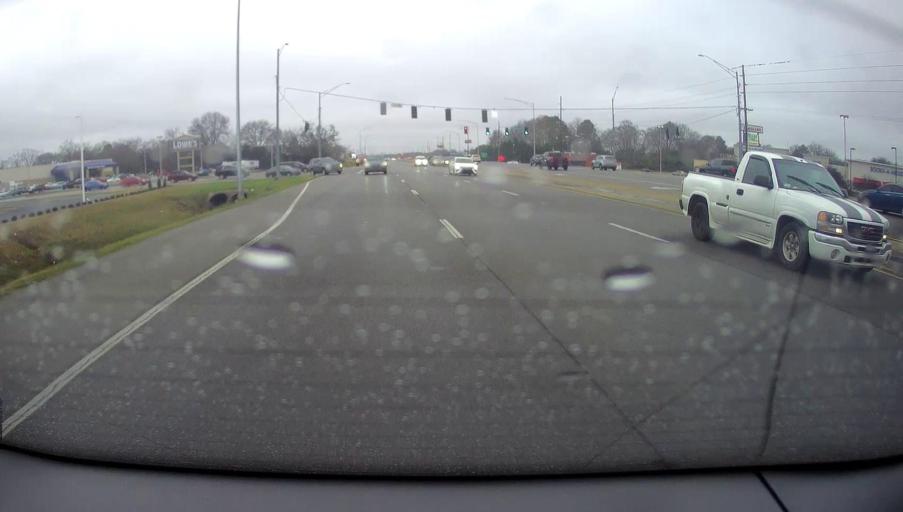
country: US
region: Alabama
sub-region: Morgan County
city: Decatur
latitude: 34.5672
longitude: -87.0117
